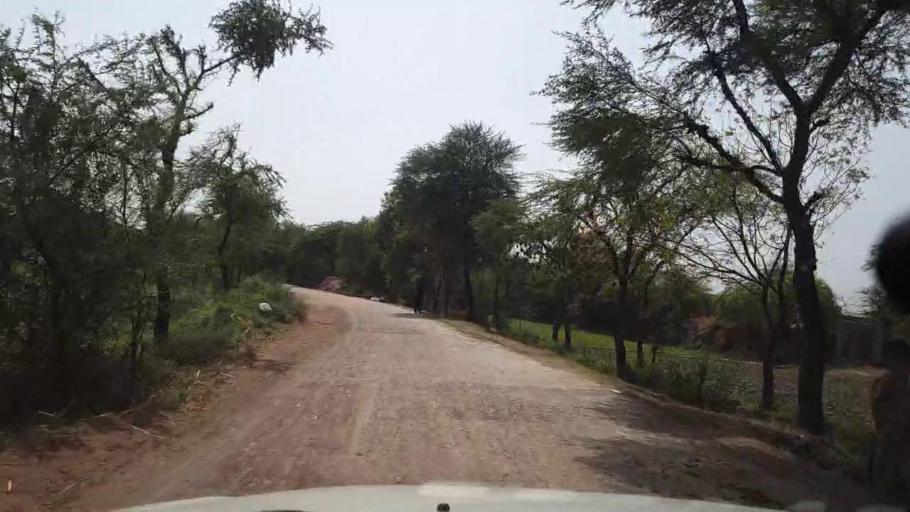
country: PK
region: Sindh
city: Matli
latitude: 25.0273
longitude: 68.7049
